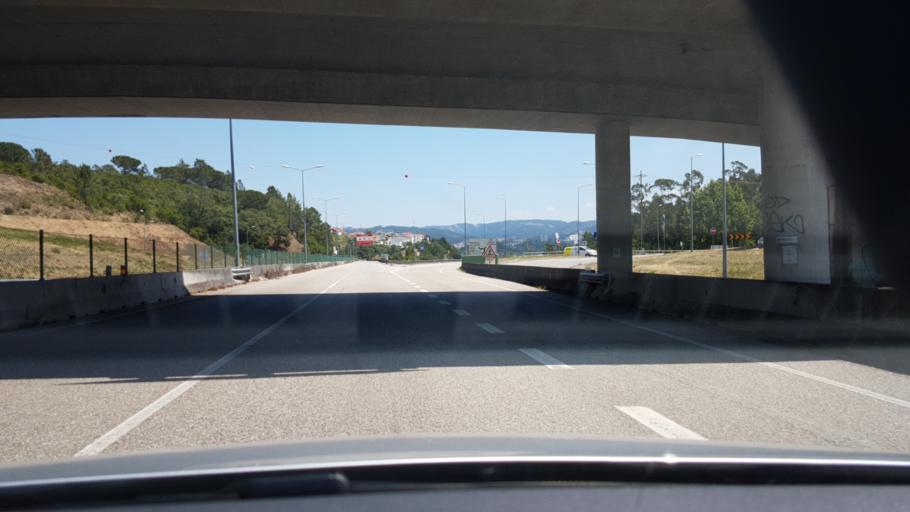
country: PT
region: Coimbra
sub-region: Coimbra
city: Coimbra
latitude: 40.1810
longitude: -8.4438
